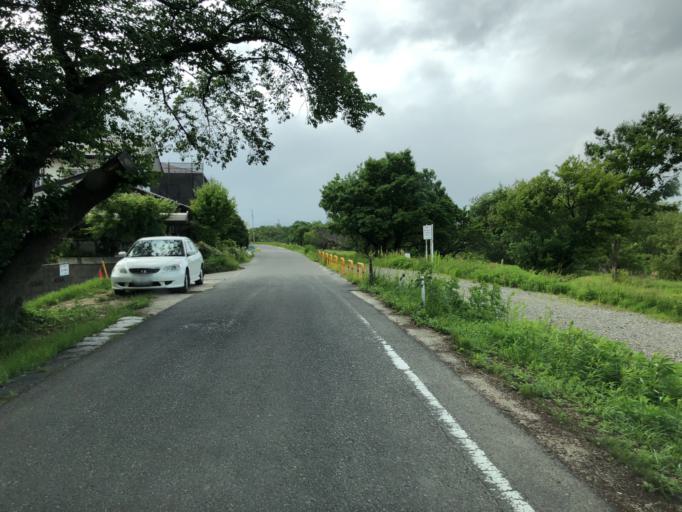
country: JP
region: Fukushima
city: Fukushima-shi
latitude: 37.7799
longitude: 140.4815
